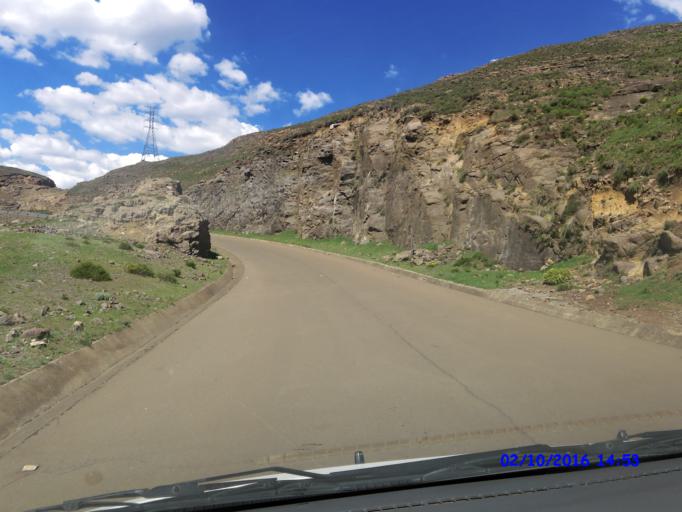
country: LS
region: Maseru
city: Nako
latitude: -29.4772
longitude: 28.0820
